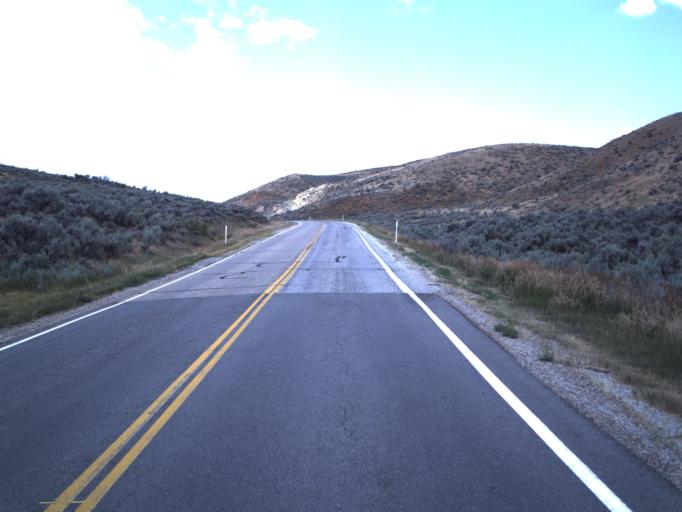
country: US
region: Utah
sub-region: Rich County
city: Randolph
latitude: 41.7795
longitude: -111.1961
